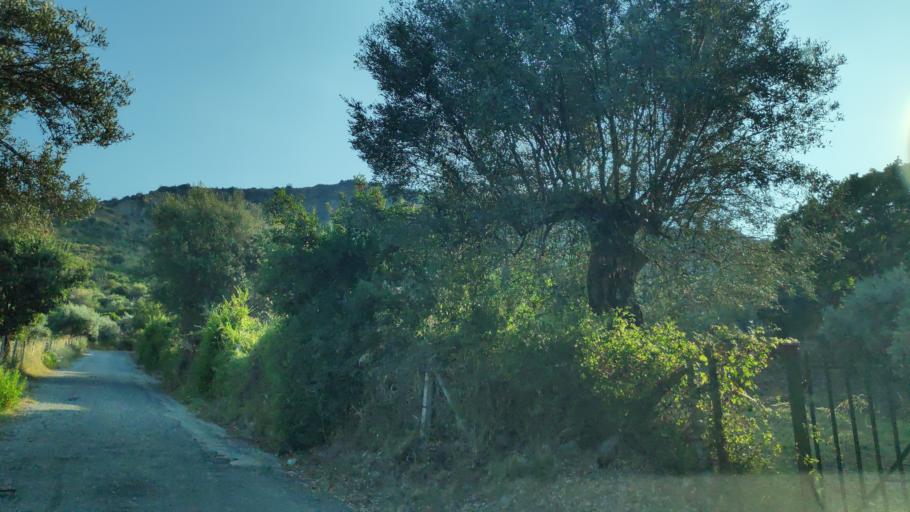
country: IT
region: Calabria
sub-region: Provincia di Reggio Calabria
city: Placanica
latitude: 38.4116
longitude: 16.4367
